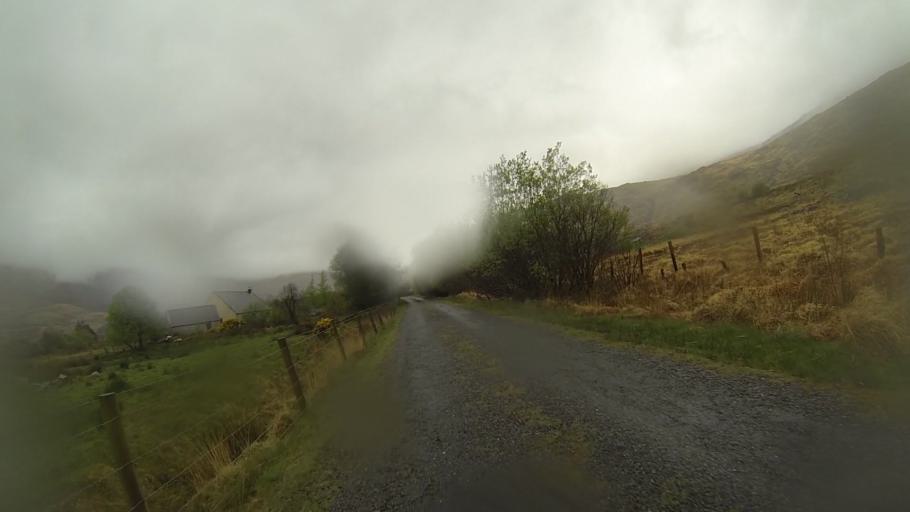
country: IE
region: Munster
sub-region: Ciarrai
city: Kenmare
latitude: 51.9502
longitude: -9.6819
